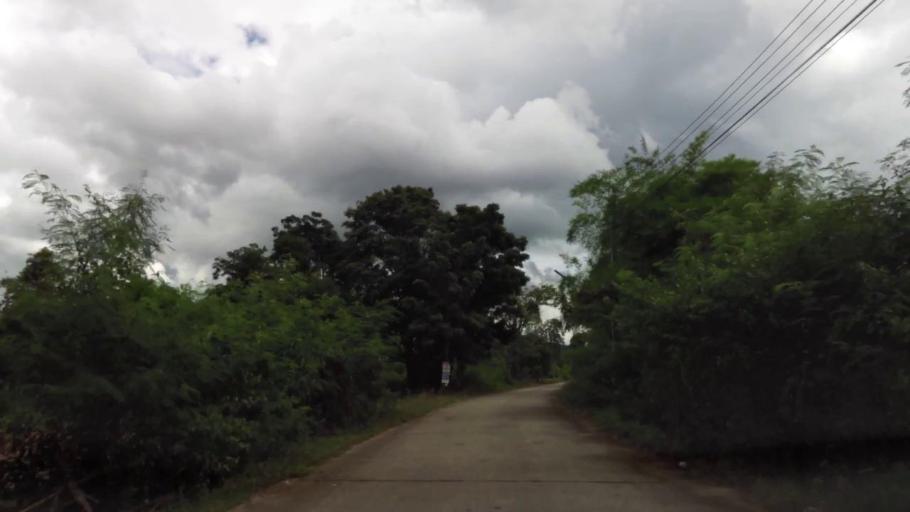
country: TH
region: Nakhon Sawan
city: Phai Sali
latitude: 15.6035
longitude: 100.6583
